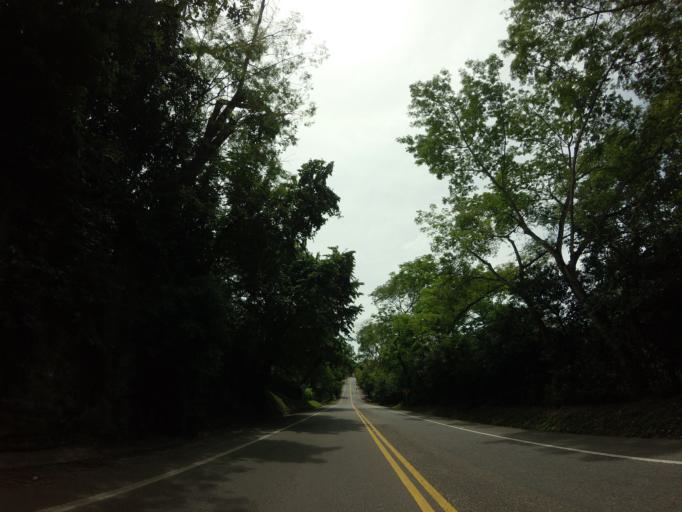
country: CO
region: Caldas
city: La Dorada
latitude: 5.4406
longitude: -74.6789
